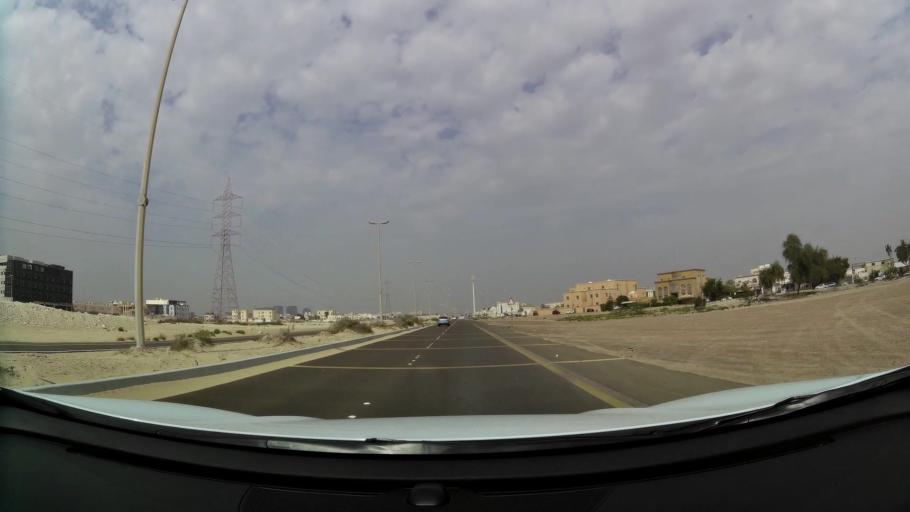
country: AE
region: Abu Dhabi
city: Abu Dhabi
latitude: 24.3184
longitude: 54.6333
